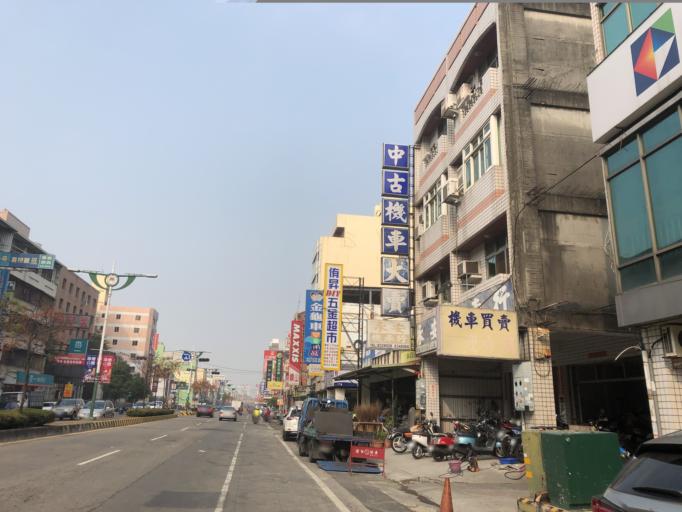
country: TW
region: Taiwan
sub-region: Nantou
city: Nantou
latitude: 23.9583
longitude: 120.5667
